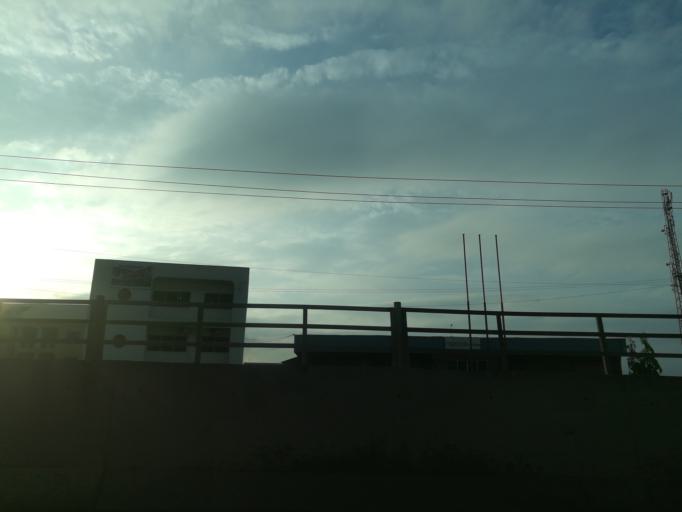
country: NG
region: Lagos
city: Ojota
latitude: 6.6054
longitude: 3.3918
